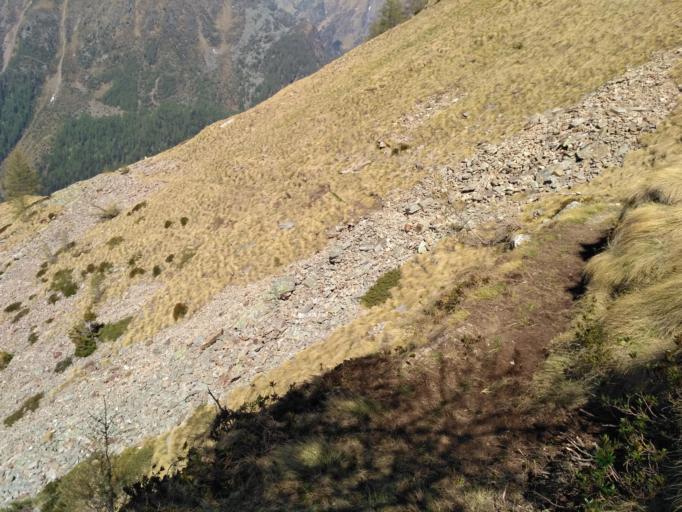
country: CH
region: Grisons
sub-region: Bernina District
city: Poschiavo
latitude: 46.2548
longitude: 10.0413
